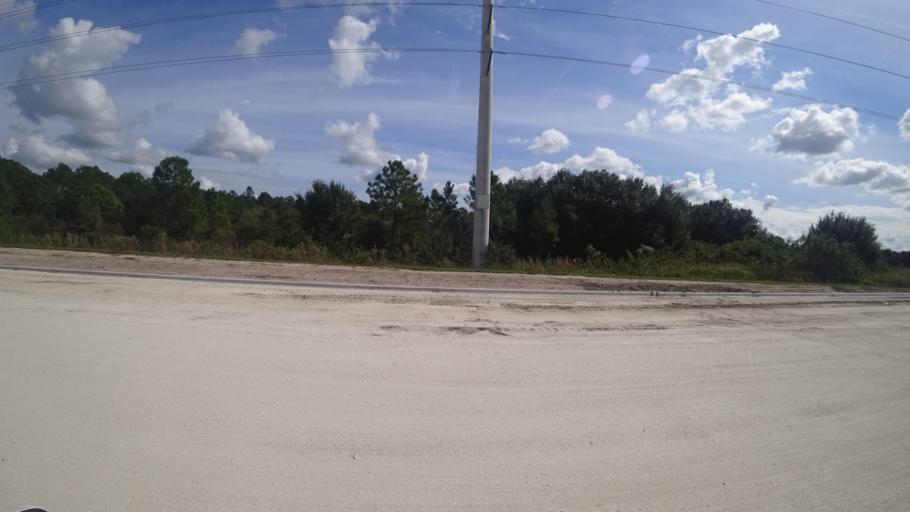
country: US
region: Florida
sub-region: Sarasota County
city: The Meadows
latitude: 27.4175
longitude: -82.3533
